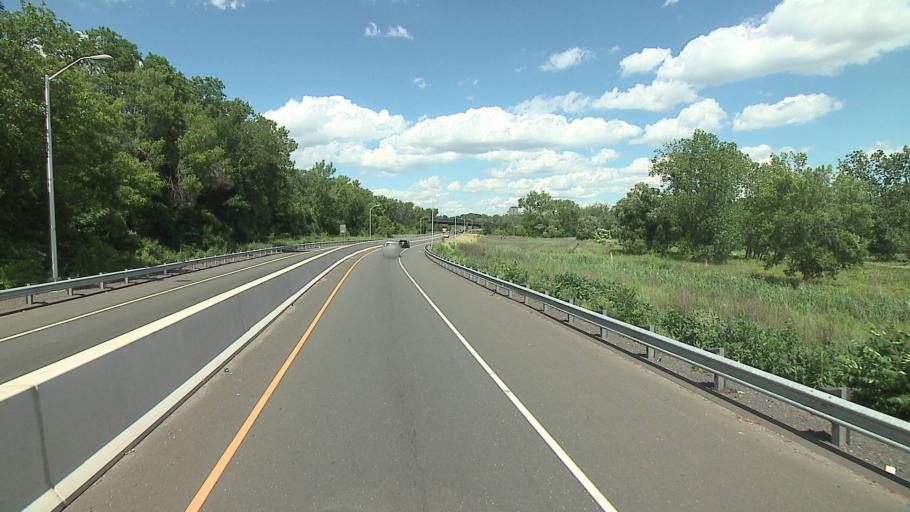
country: US
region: Connecticut
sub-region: Hartford County
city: Hartford
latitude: 41.7472
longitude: -72.7091
